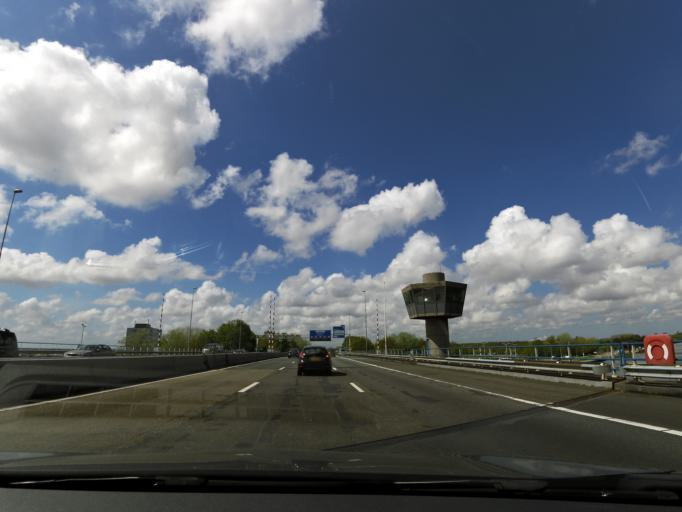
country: NL
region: North Holland
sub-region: Gemeente Amstelveen
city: Amstelveen
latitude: 52.3126
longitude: 4.8159
